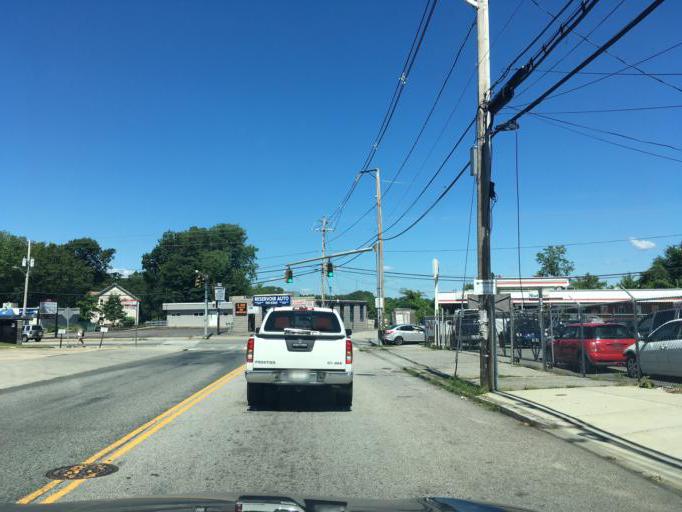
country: US
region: Rhode Island
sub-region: Providence County
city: Cranston
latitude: 41.7892
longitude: -71.4292
